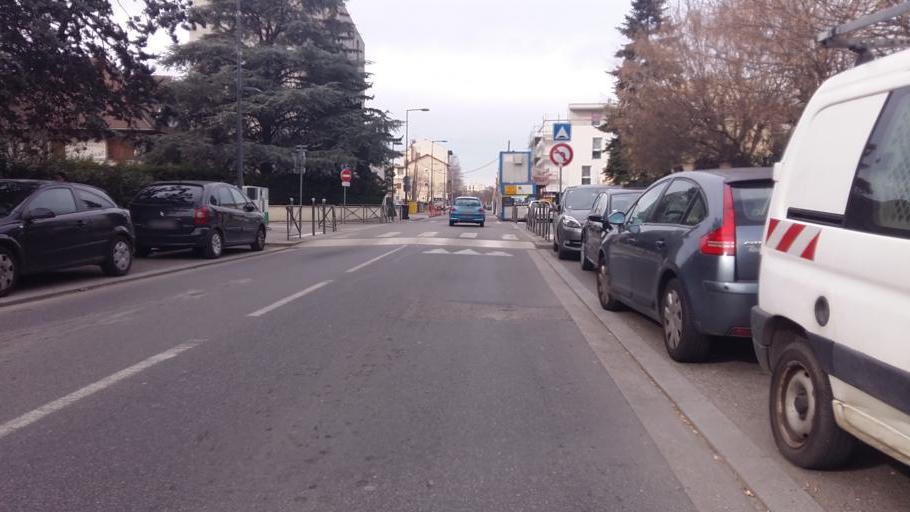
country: FR
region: Rhone-Alpes
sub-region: Departement du Rhone
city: Villeurbanne
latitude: 45.7772
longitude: 4.8924
